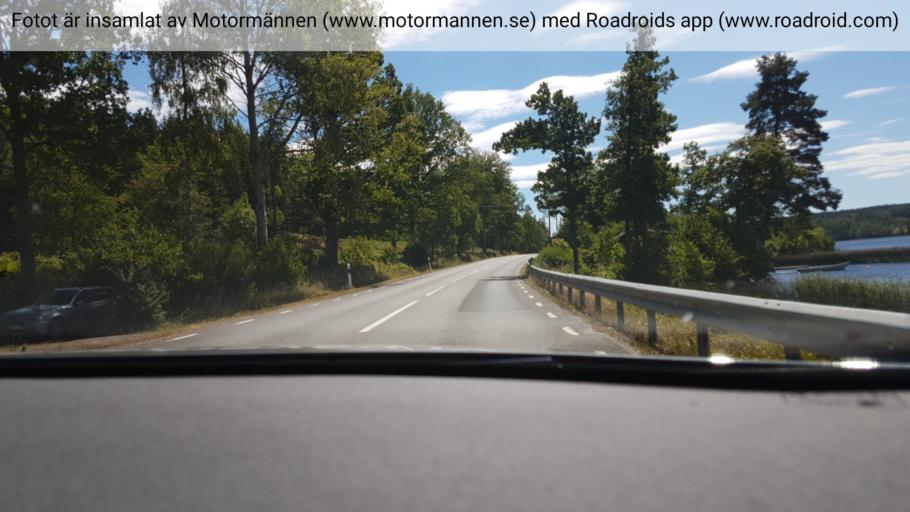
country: SE
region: Joenkoeping
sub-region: Jonkopings Kommun
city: Asa
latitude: 58.0109
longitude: 14.7101
